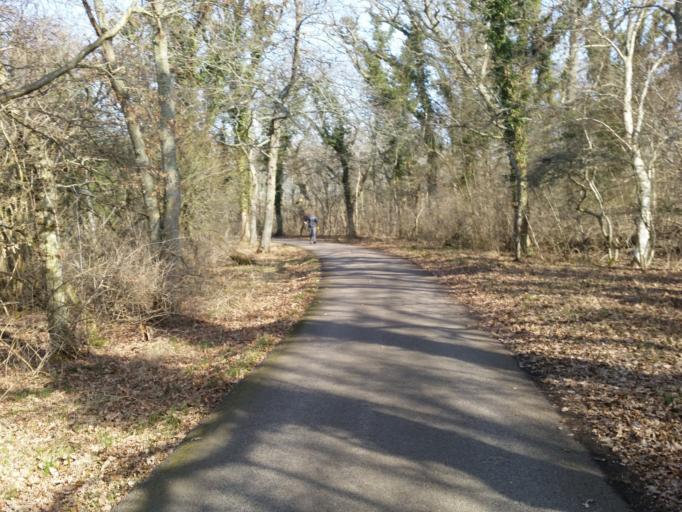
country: SE
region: Kalmar
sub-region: Borgholms Kommun
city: Borgholm
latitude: 56.8761
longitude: 16.6387
